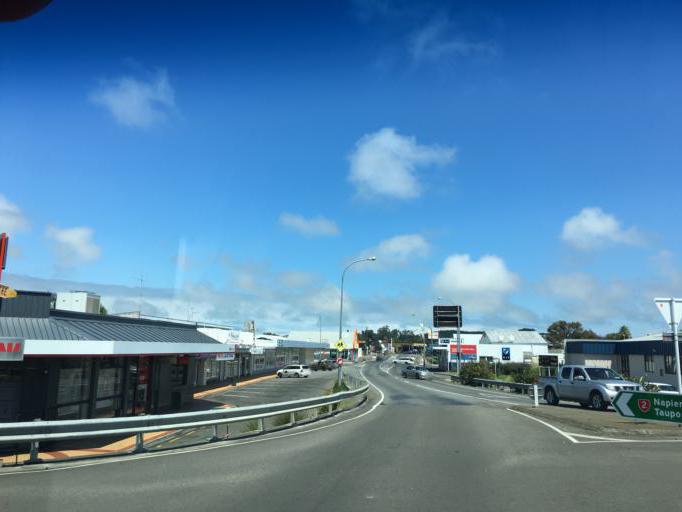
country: NZ
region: Hawke's Bay
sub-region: Wairoa District
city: Wairoa
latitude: -39.0329
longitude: 177.4185
